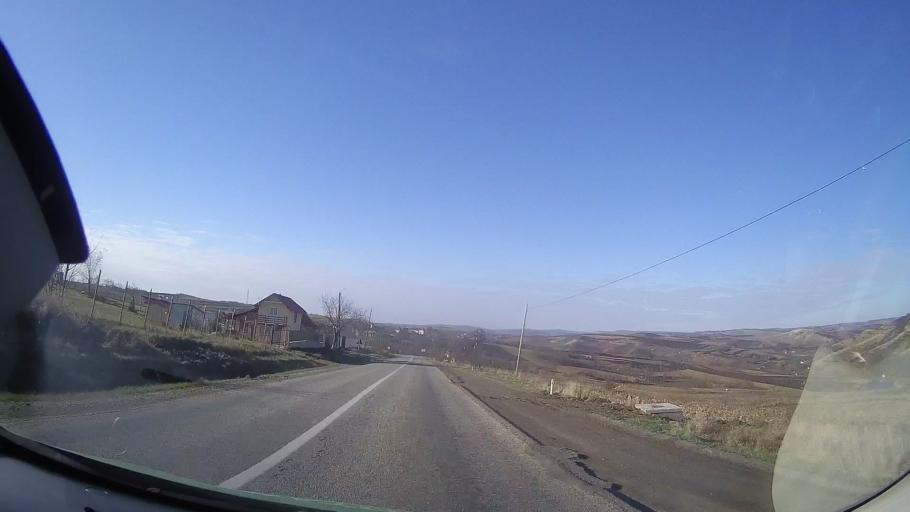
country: RO
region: Cluj
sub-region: Comuna Mociu
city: Mociu
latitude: 46.7895
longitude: 24.0809
